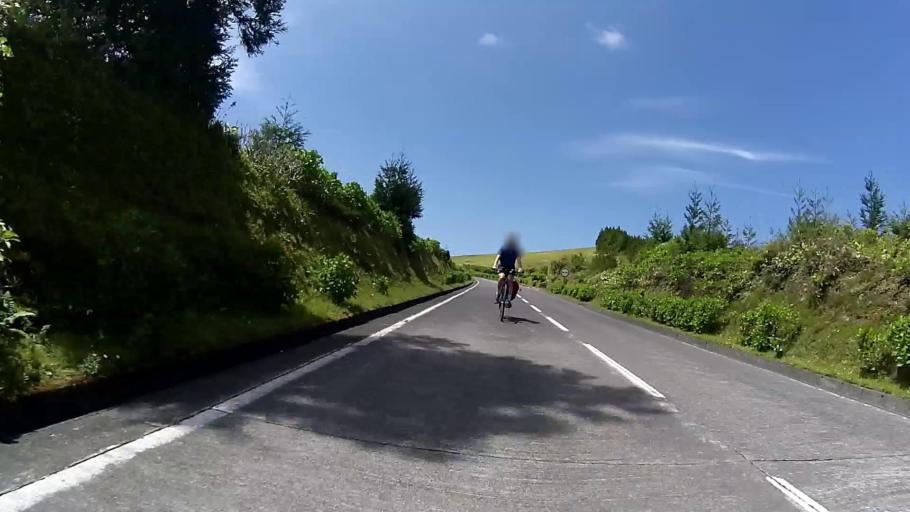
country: PT
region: Azores
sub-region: Ponta Delgada
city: Arrifes
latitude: 37.8438
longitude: -25.7715
